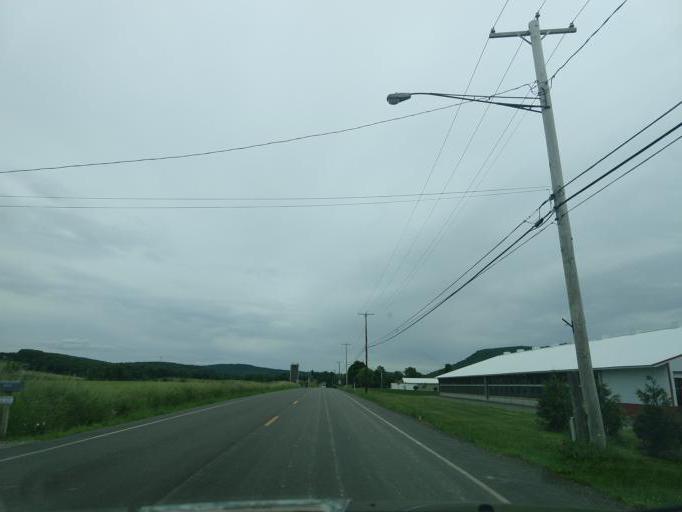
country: US
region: New York
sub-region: Cortland County
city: Munsons Corners
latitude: 42.5107
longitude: -76.1892
